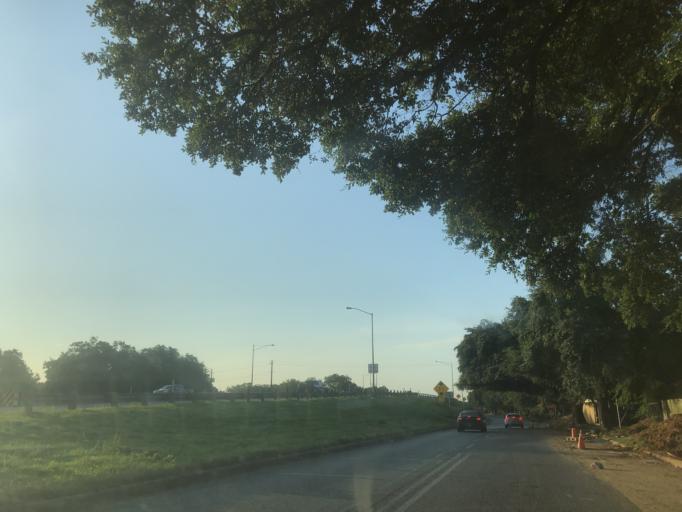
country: US
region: Texas
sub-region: Dallas County
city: Dallas
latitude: 32.7542
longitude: -96.7657
